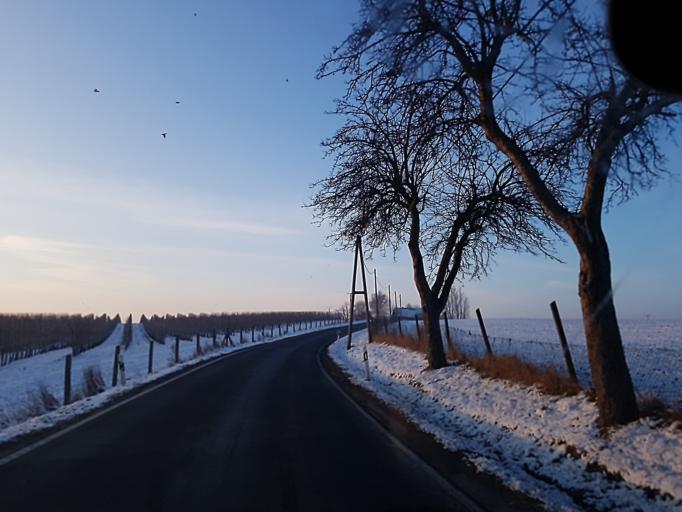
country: DE
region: Saxony
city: Mugeln
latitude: 51.2158
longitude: 13.0333
